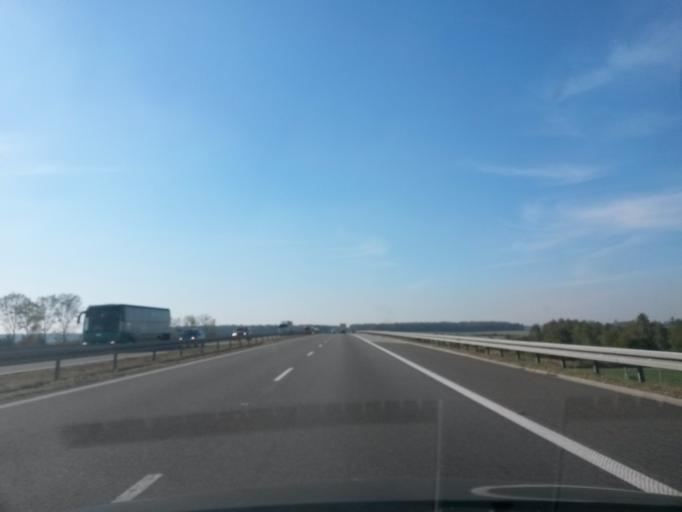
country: PL
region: Opole Voivodeship
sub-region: Powiat strzelecki
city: Ujazd
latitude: 50.4494
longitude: 18.3255
